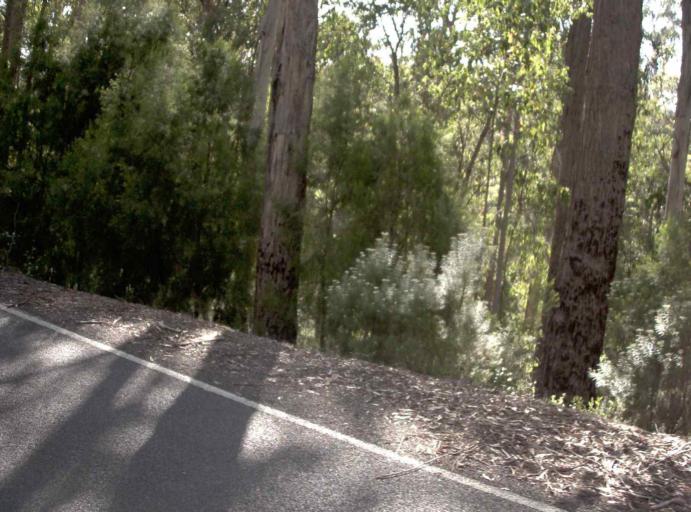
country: AU
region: Victoria
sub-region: East Gippsland
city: Lakes Entrance
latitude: -37.5865
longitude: 148.5350
